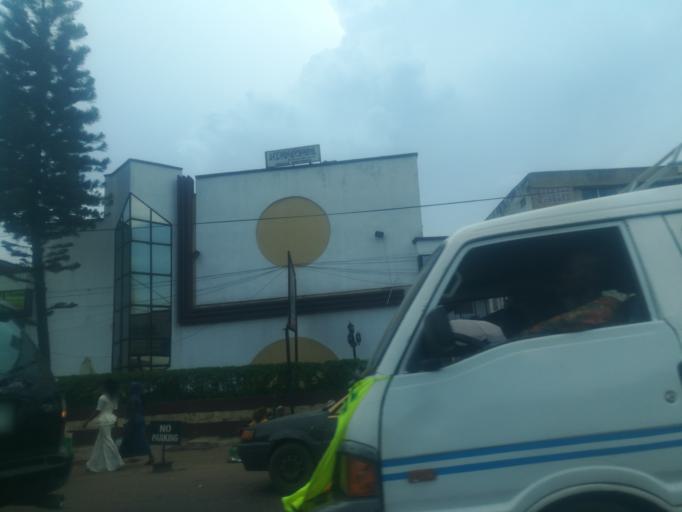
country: NG
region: Oyo
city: Ibadan
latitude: 7.4241
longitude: 3.8979
